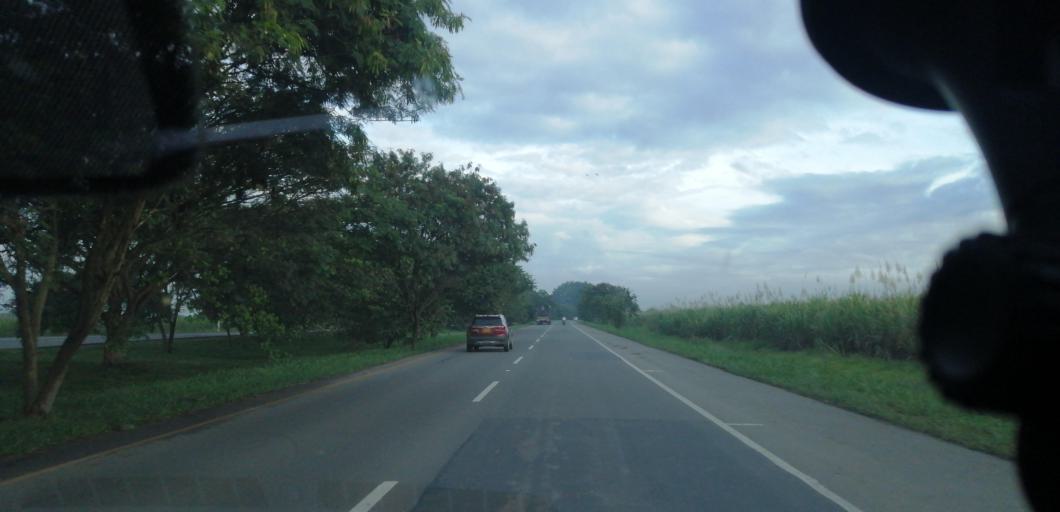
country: CO
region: Valle del Cauca
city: Palmira
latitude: 3.5345
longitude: -76.3379
